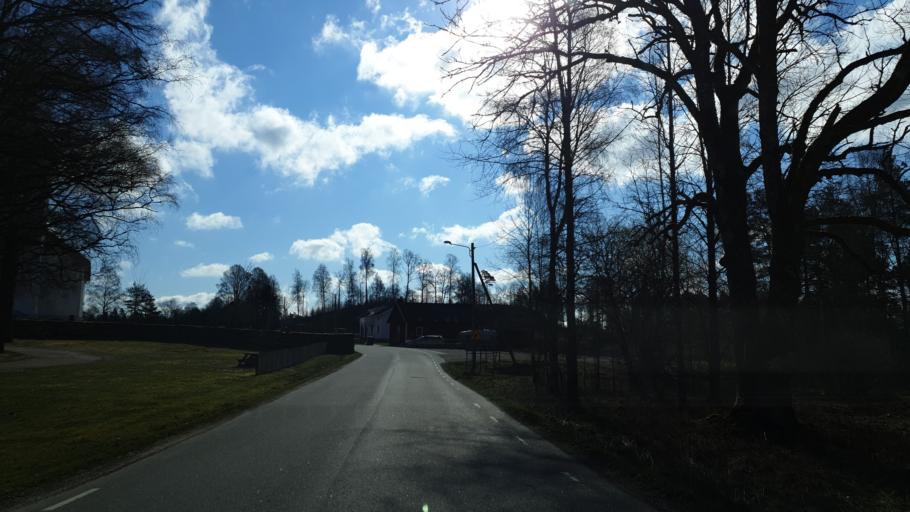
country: SE
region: Vaestra Goetaland
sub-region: Svenljunga Kommun
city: Svenljunga
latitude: 57.4423
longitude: 13.1208
